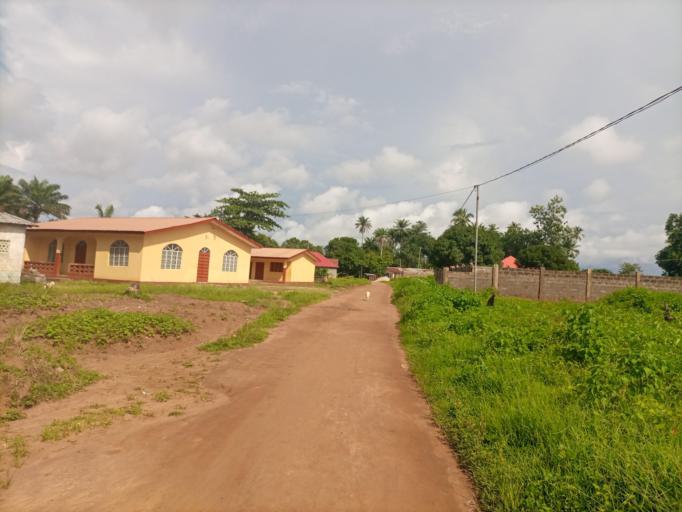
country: SL
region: Northern Province
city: Masoyila
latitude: 8.6264
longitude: -13.1767
